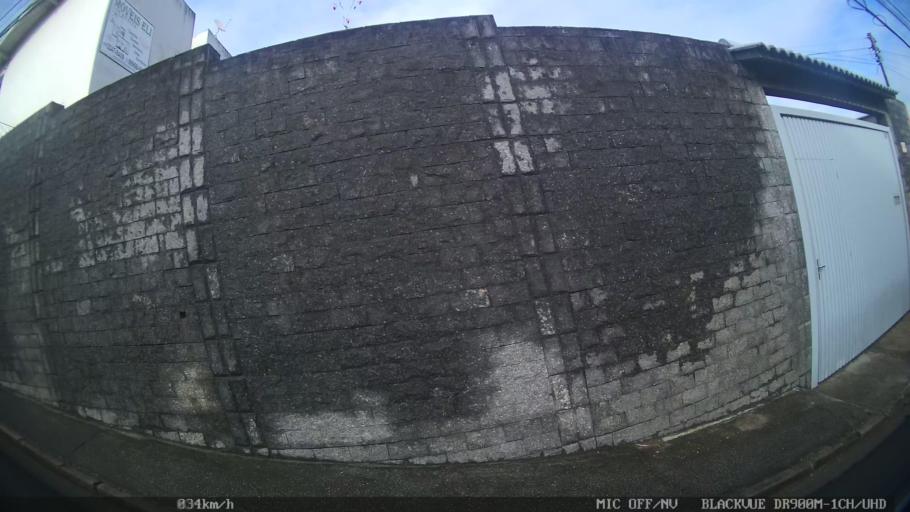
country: BR
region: Santa Catarina
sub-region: Sao Jose
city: Campinas
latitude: -27.6125
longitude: -48.6297
